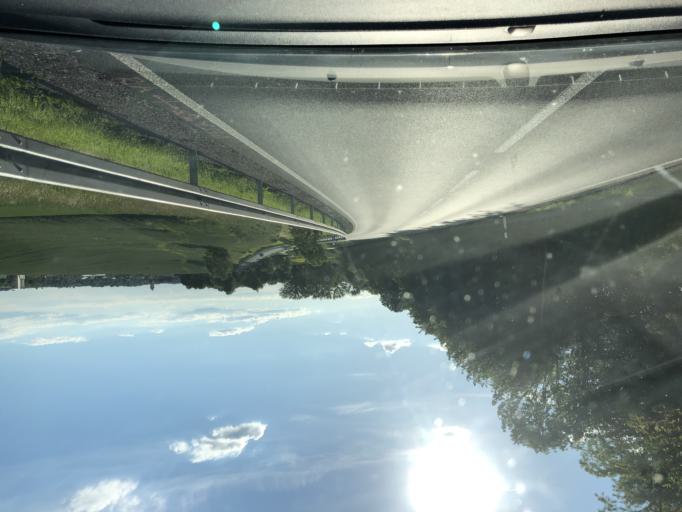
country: DE
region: Thuringia
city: Lodla
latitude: 51.0018
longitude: 12.4004
